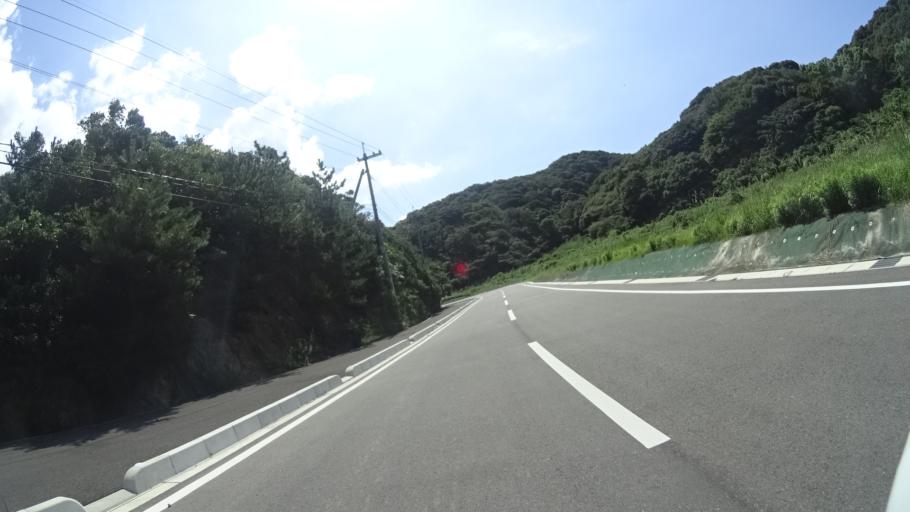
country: JP
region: Yamaguchi
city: Shimonoseki
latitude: 34.0973
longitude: 130.8756
